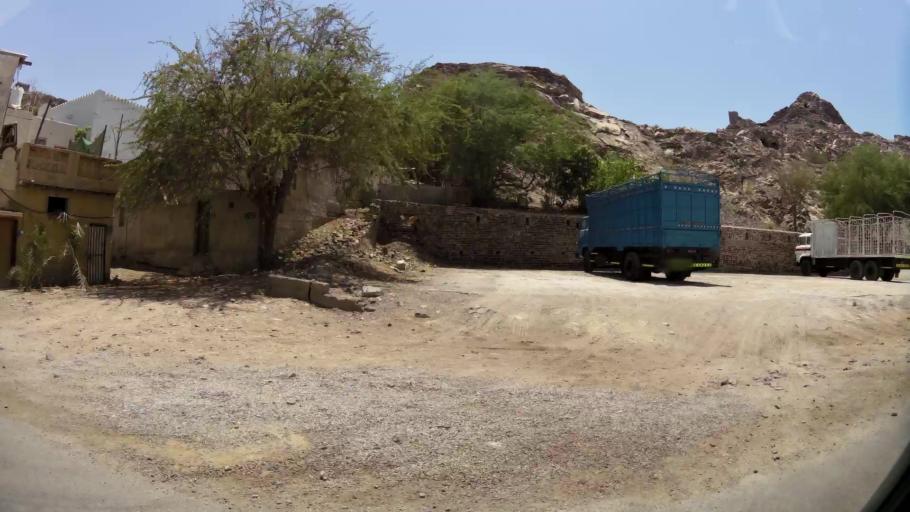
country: OM
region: Muhafazat Masqat
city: Muscat
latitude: 23.6128
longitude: 58.5877
